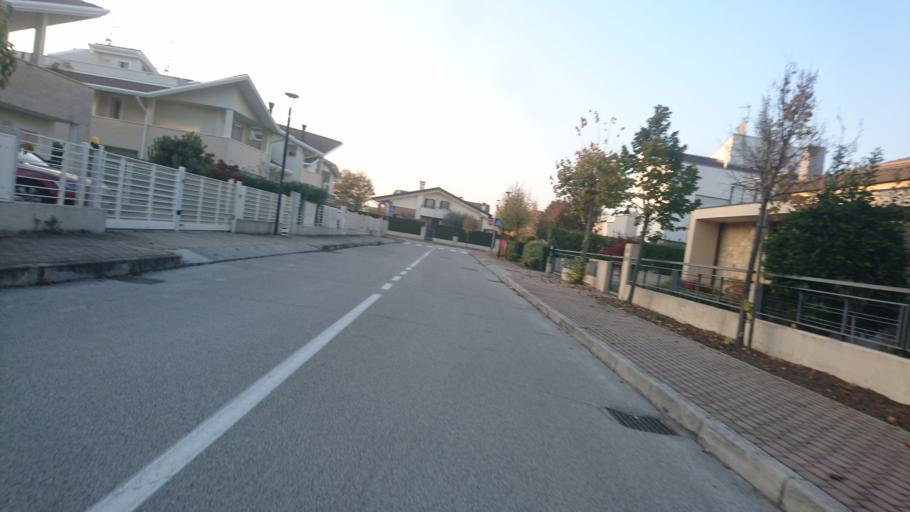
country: IT
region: Veneto
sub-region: Provincia di Padova
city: Abano Terme
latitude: 45.3443
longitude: 11.7937
